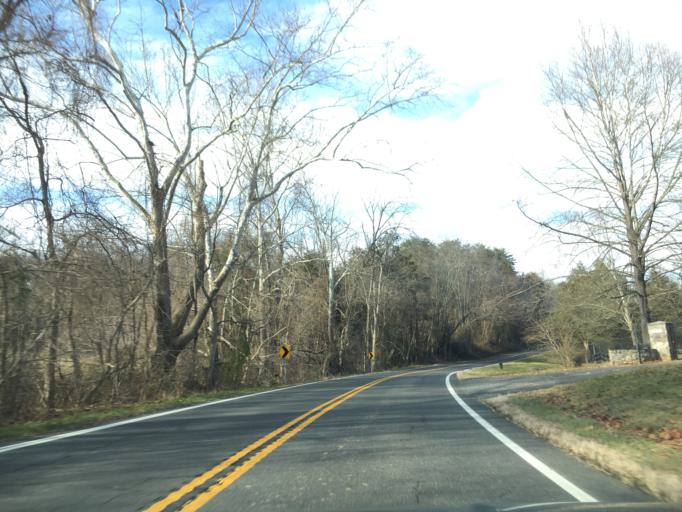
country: US
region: Virginia
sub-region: Fauquier County
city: Warrenton
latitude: 38.7002
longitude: -77.9103
